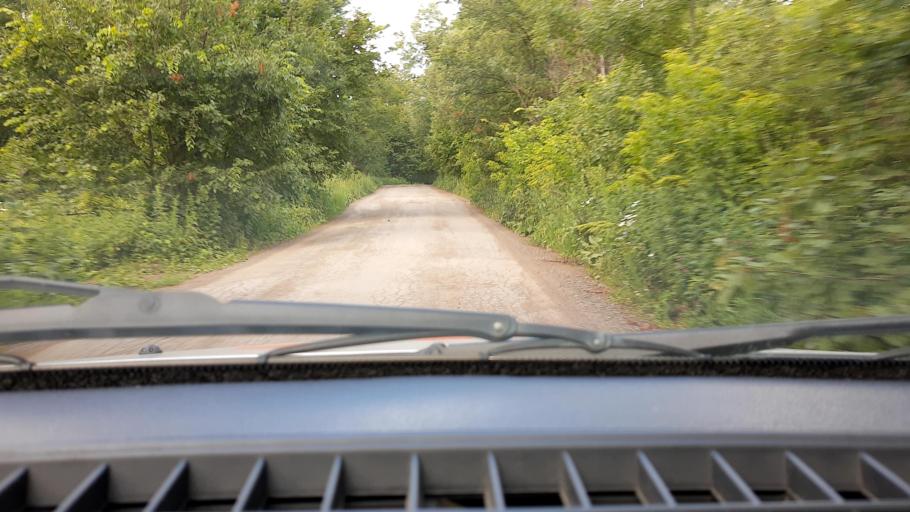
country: RU
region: Bashkortostan
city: Ufa
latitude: 54.6848
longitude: 56.0586
